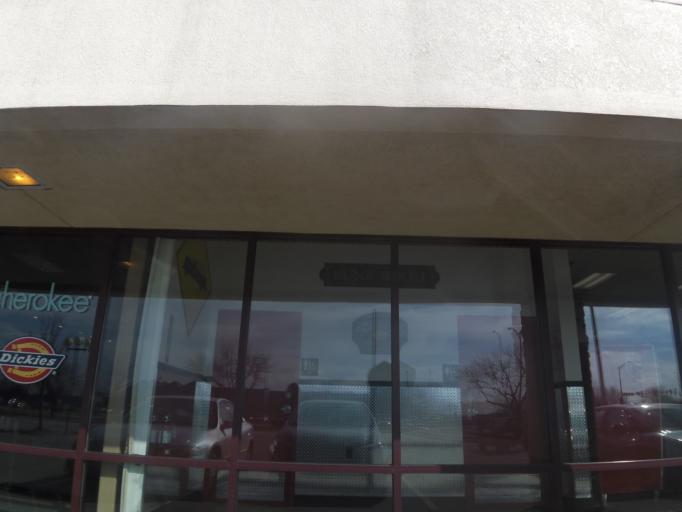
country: US
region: North Dakota
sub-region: Grand Forks County
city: Grand Forks
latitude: 47.8901
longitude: -97.0660
